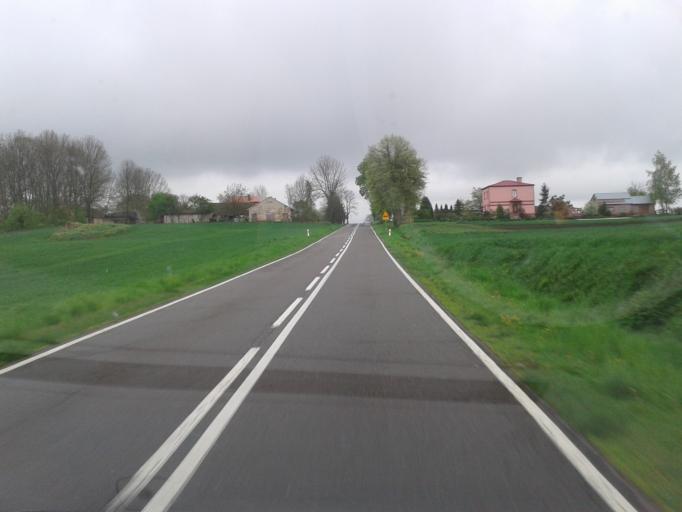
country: PL
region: Lublin Voivodeship
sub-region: Powiat hrubieszowski
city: Dolhobyczow
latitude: 50.5805
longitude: 23.9676
